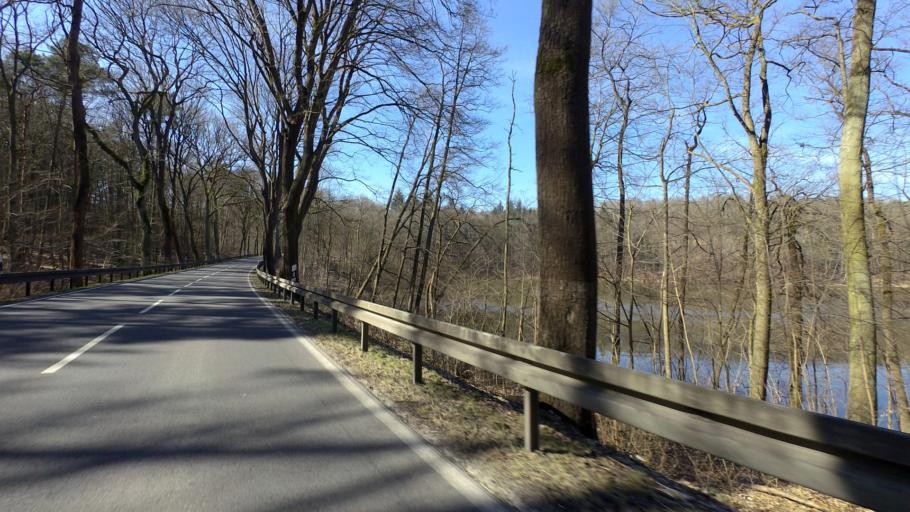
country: DE
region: Brandenburg
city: Waldsieversdorf
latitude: 52.5280
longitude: 14.0801
